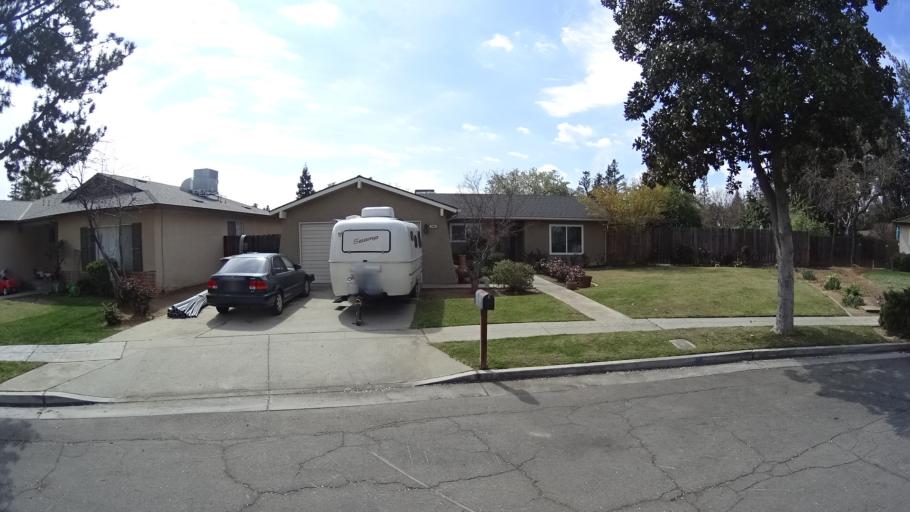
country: US
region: California
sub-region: Fresno County
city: Fresno
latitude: 36.8212
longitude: -119.8553
